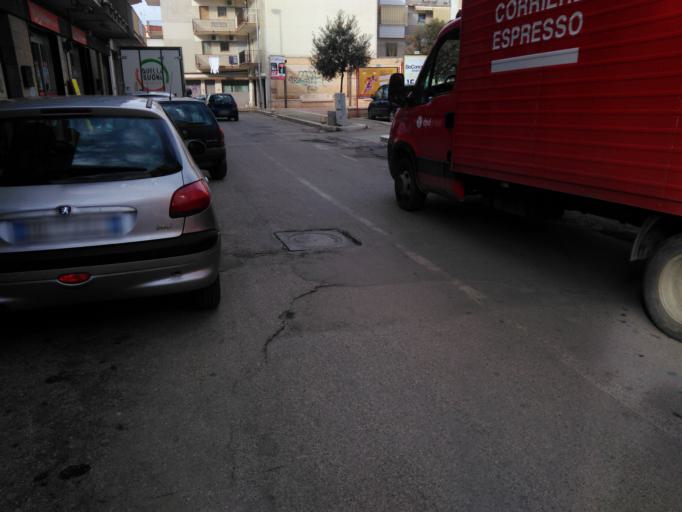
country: IT
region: Apulia
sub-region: Provincia di Barletta - Andria - Trani
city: Andria
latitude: 41.2335
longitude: 16.2975
